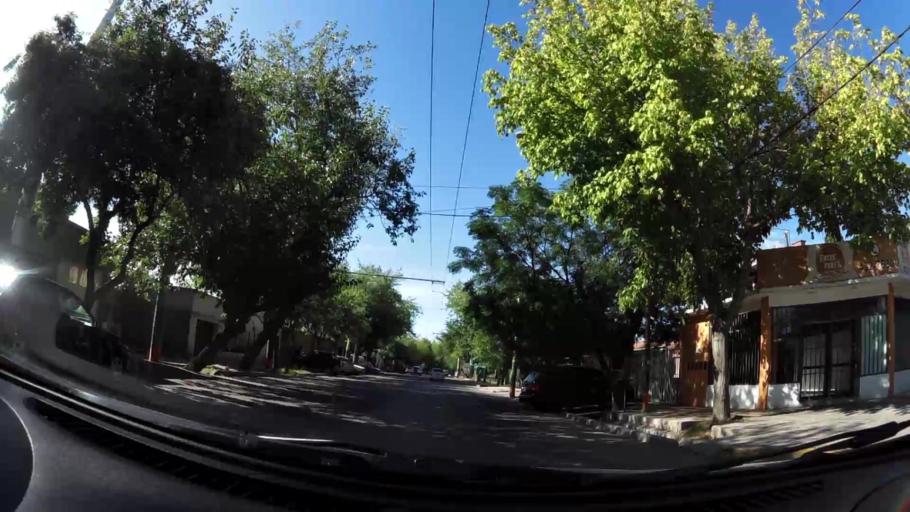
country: AR
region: Mendoza
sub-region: Departamento de Godoy Cruz
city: Godoy Cruz
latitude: -32.9103
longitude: -68.8327
